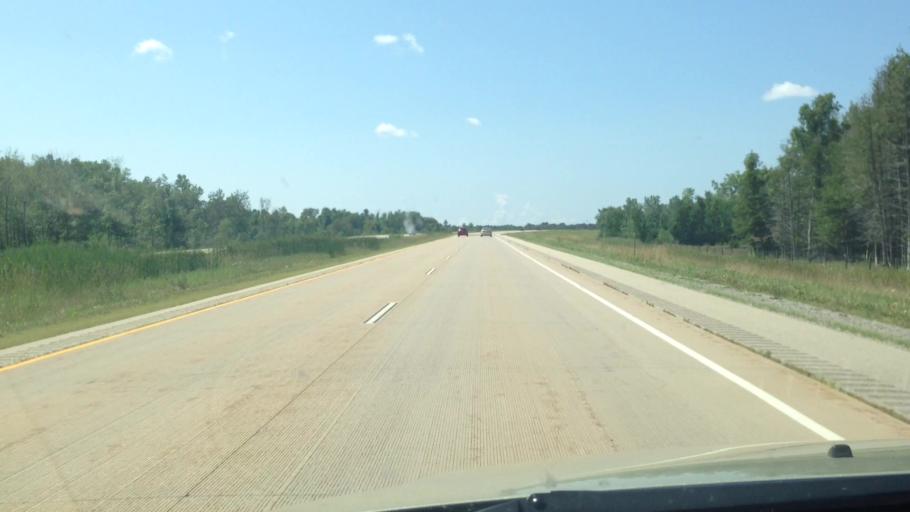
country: US
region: Wisconsin
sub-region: Oconto County
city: Oconto
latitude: 44.9120
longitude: -87.8792
